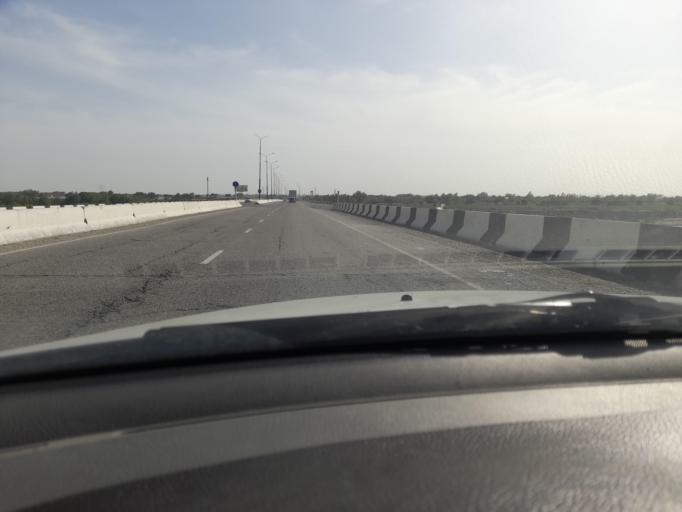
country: UZ
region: Samarqand
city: Kattaqo'rg'on
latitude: 39.9302
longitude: 66.3625
